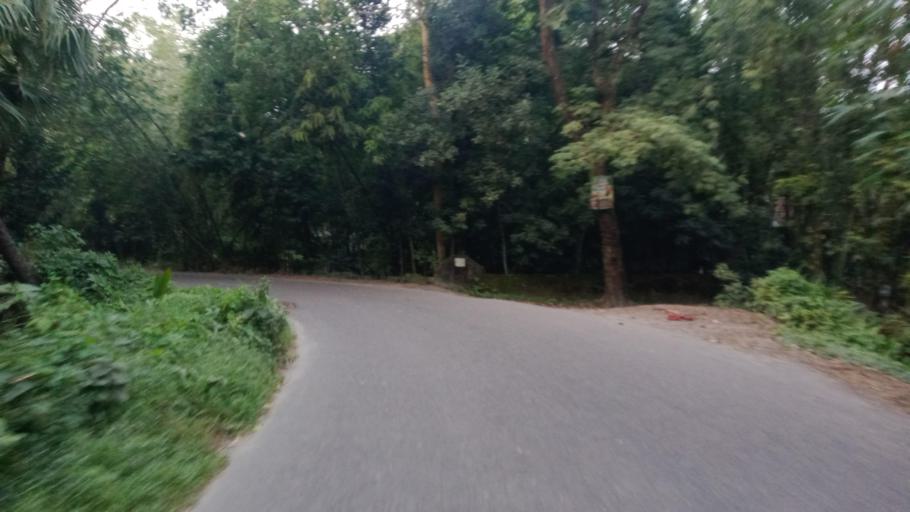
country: BD
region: Chittagong
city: Hajiganj
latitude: 23.3692
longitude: 90.9838
